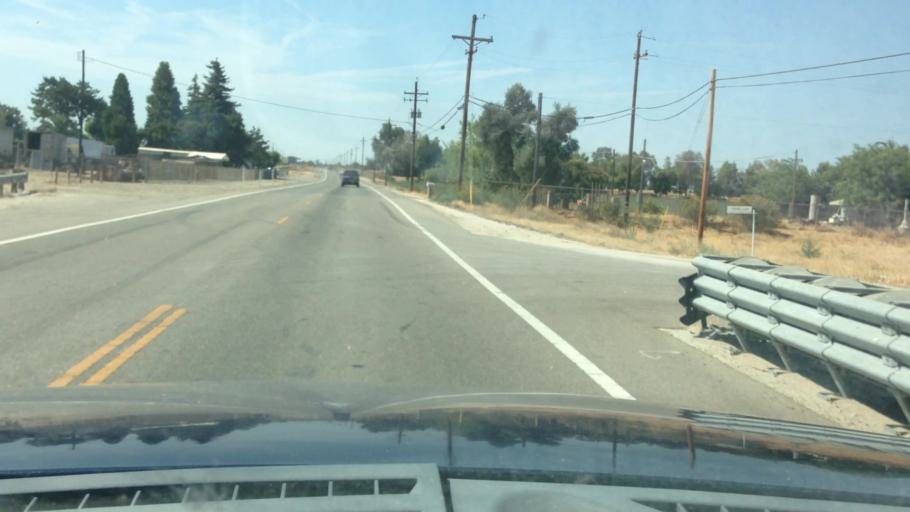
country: US
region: California
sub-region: Fresno County
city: Parlier
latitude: 36.5984
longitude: -119.5569
